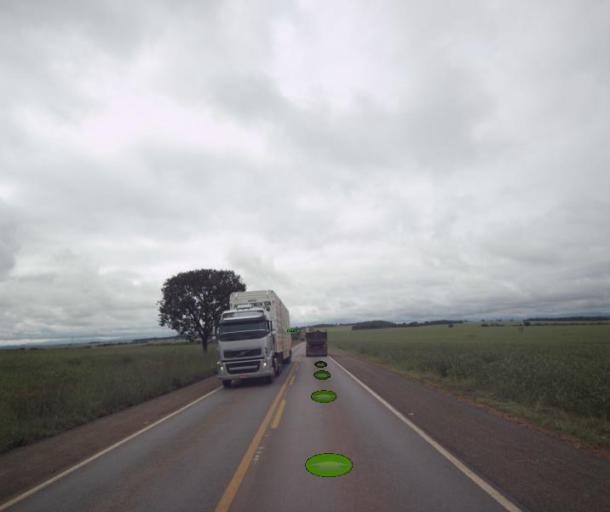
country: BR
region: Goias
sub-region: Uruacu
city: Uruacu
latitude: -14.6632
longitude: -49.1531
